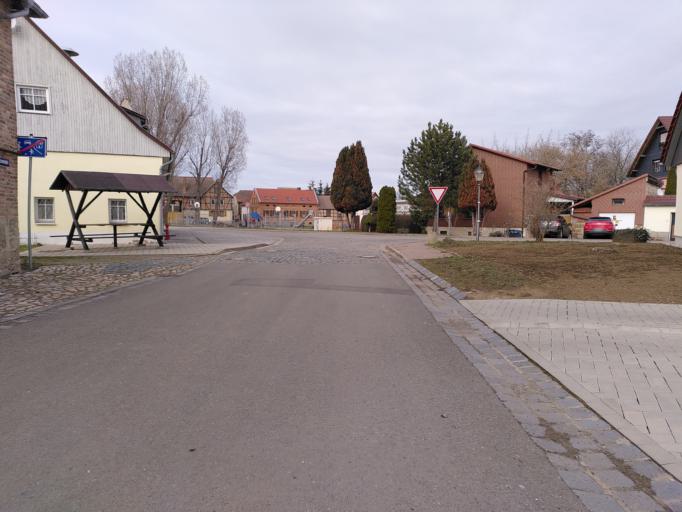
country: DE
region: Saxony-Anhalt
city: Ballenstedt
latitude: 51.7655
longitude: 11.2409
